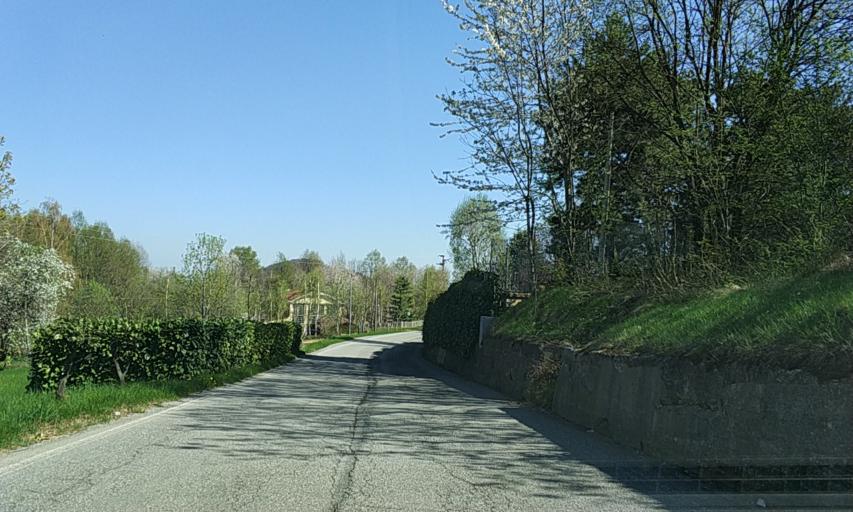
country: IT
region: Piedmont
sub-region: Provincia di Torino
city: Forno Canavese
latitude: 45.3378
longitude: 7.5915
